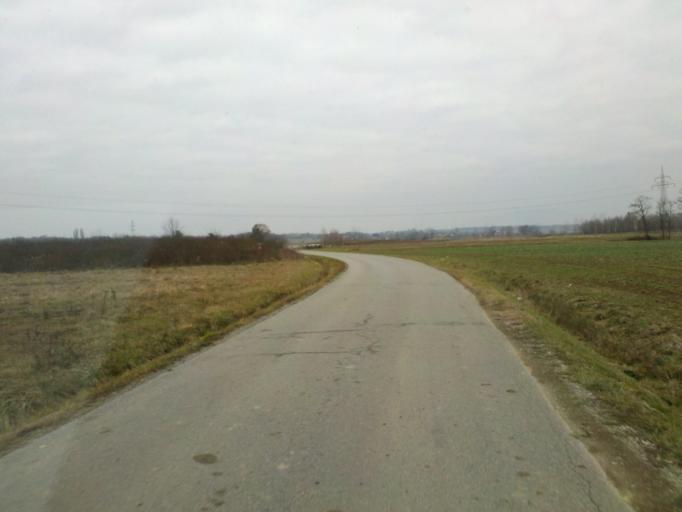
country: HR
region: Grad Zagreb
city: Strmec
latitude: 45.6847
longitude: 15.8726
